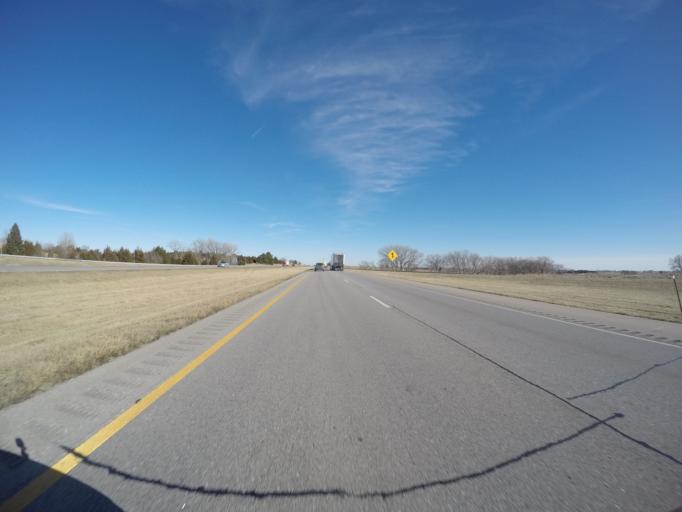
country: US
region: Nebraska
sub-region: Seward County
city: Milford
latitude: 40.8211
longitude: -96.9277
